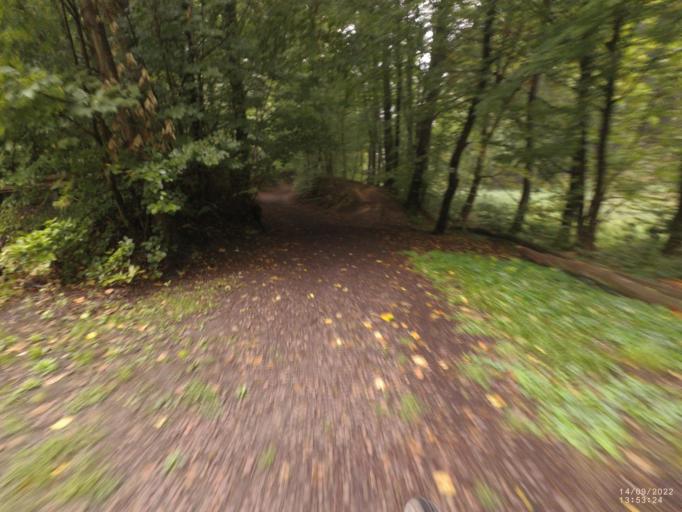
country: DE
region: Bavaria
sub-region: Regierungsbezirk Unterfranken
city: Glattbach
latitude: 50.0121
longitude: 9.1432
